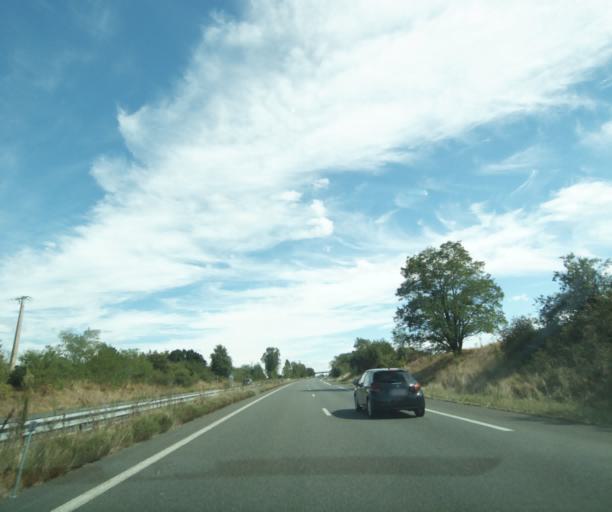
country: FR
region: Midi-Pyrenees
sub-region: Departement du Tarn-et-Garonne
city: Auvillar
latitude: 44.0573
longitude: 0.9476
